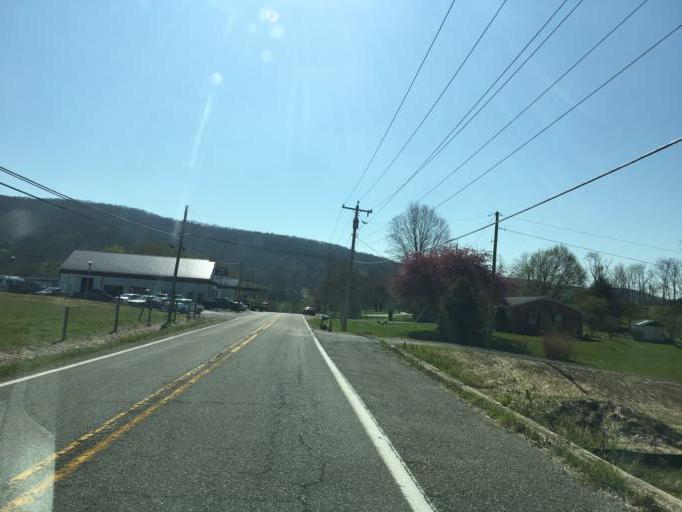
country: US
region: Maryland
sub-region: Frederick County
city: Myersville
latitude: 39.5651
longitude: -77.5293
